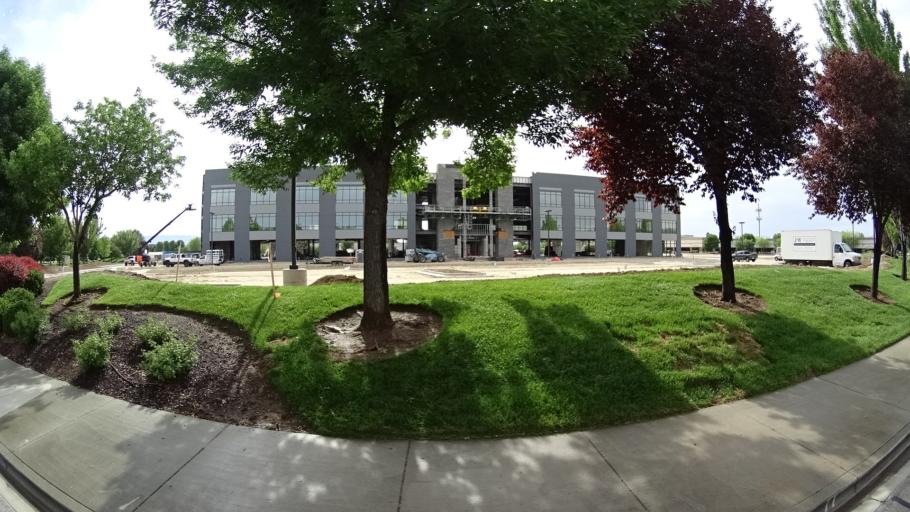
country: US
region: Idaho
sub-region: Ada County
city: Meridian
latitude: 43.5879
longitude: -116.3519
